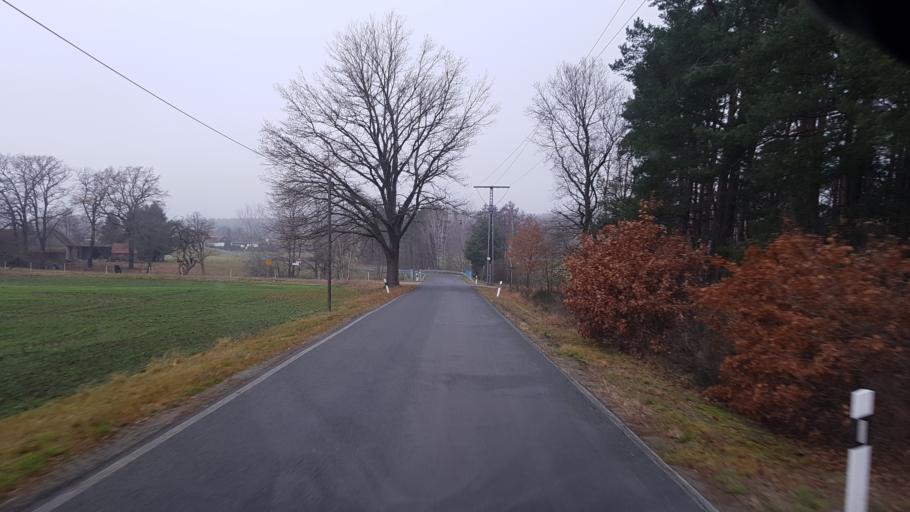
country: DE
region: Brandenburg
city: Calau
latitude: 51.6870
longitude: 13.9761
